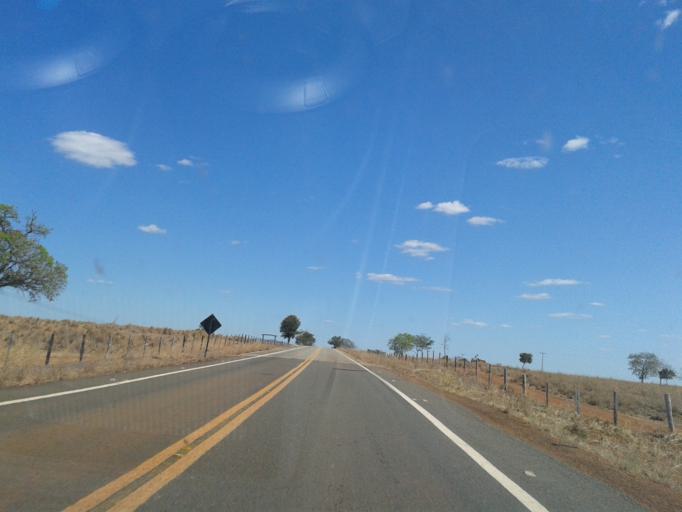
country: BR
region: Goias
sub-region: Sao Miguel Do Araguaia
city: Sao Miguel do Araguaia
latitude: -13.4026
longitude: -50.2597
